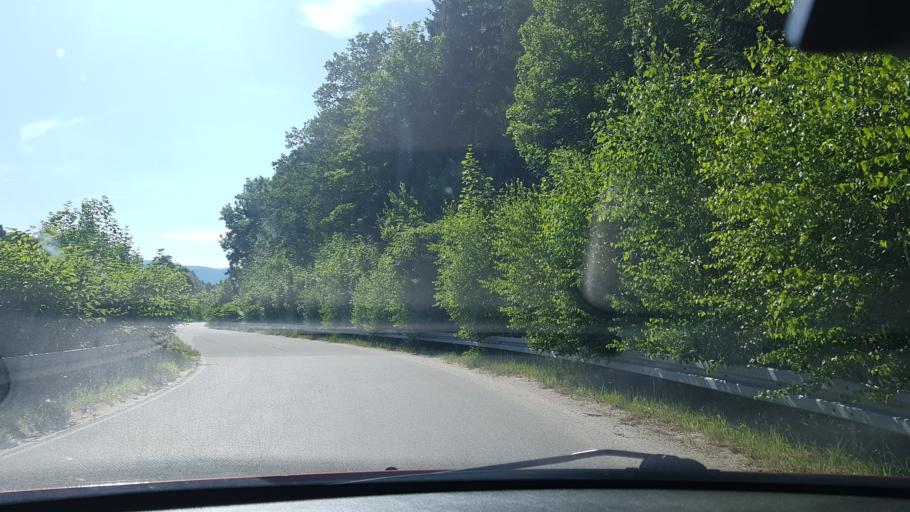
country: PL
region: Lower Silesian Voivodeship
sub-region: Powiat klodzki
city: Miedzylesie
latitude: 50.2330
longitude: 16.7415
